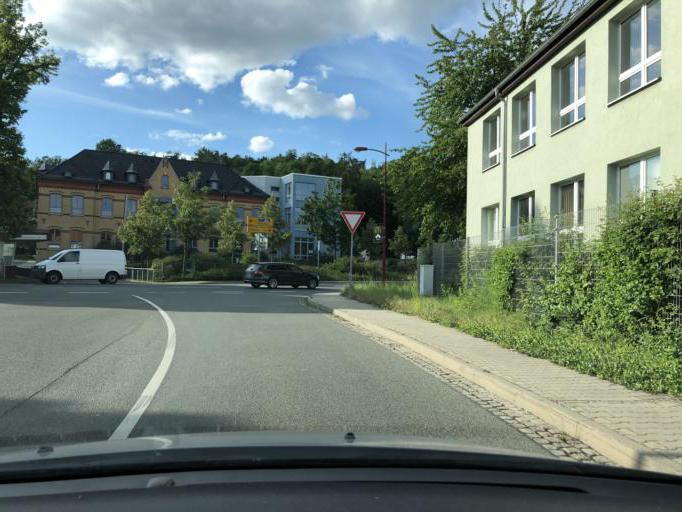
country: DE
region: Thuringia
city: Schmolln
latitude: 50.9040
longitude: 12.3610
